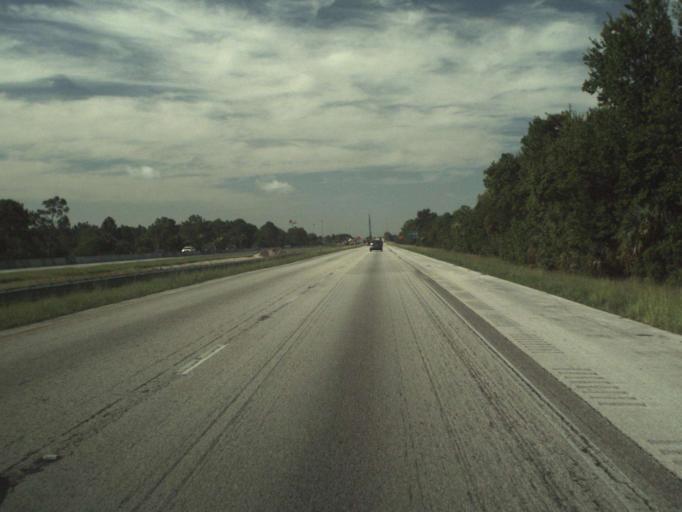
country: US
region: Florida
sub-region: Indian River County
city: Fellsmere
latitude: 27.7794
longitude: -80.5506
